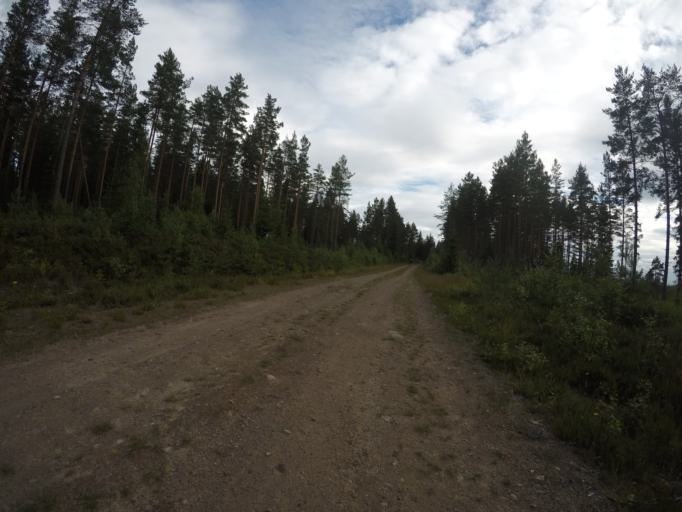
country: SE
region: Vaermland
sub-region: Filipstads Kommun
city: Lesjofors
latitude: 60.0209
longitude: 14.3959
